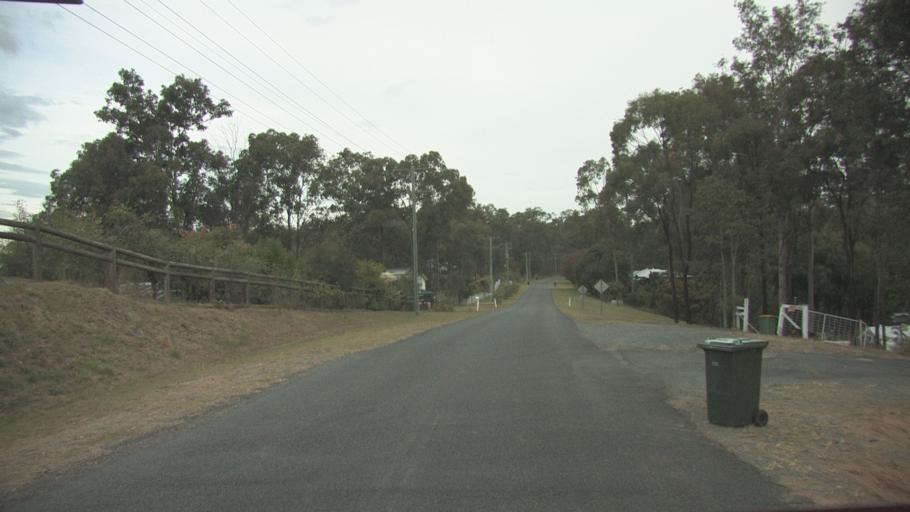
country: AU
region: Queensland
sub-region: Logan
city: Chambers Flat
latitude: -27.8231
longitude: 153.0955
